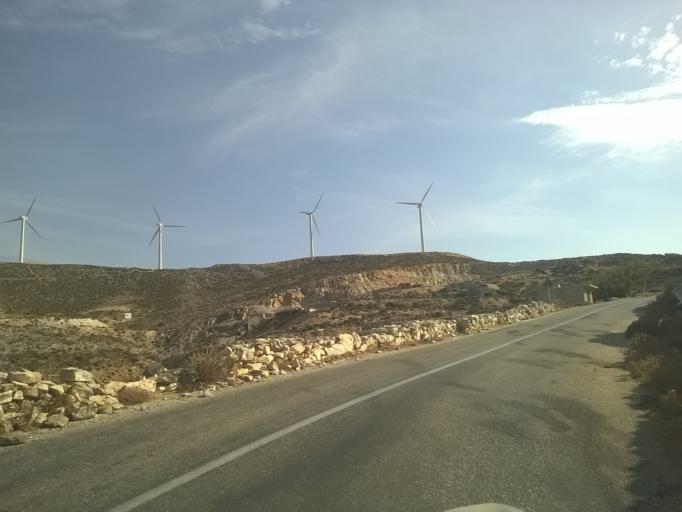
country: GR
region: South Aegean
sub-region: Nomos Kykladon
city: Filotion
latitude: 37.1157
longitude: 25.5397
